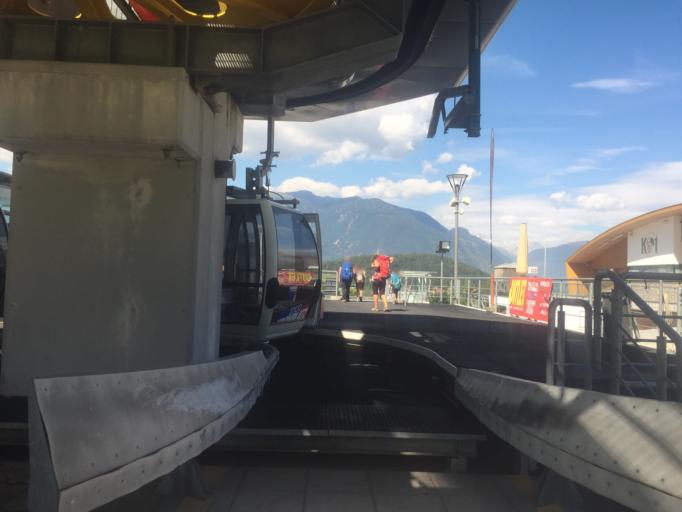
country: IT
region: Trentino-Alto Adige
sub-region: Bolzano
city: Riscone
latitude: 46.7719
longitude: 11.9411
